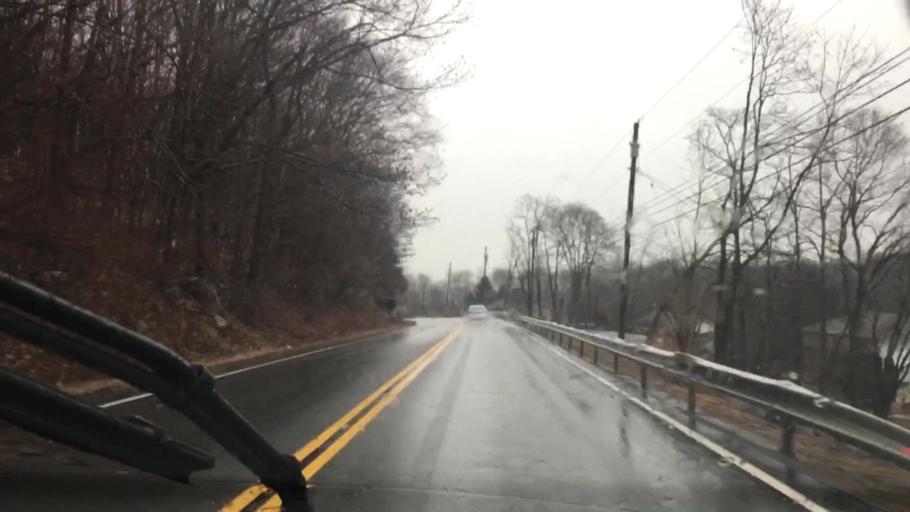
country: US
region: New York
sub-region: Putnam County
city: Putnam Lake
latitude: 41.4759
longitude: -73.5678
